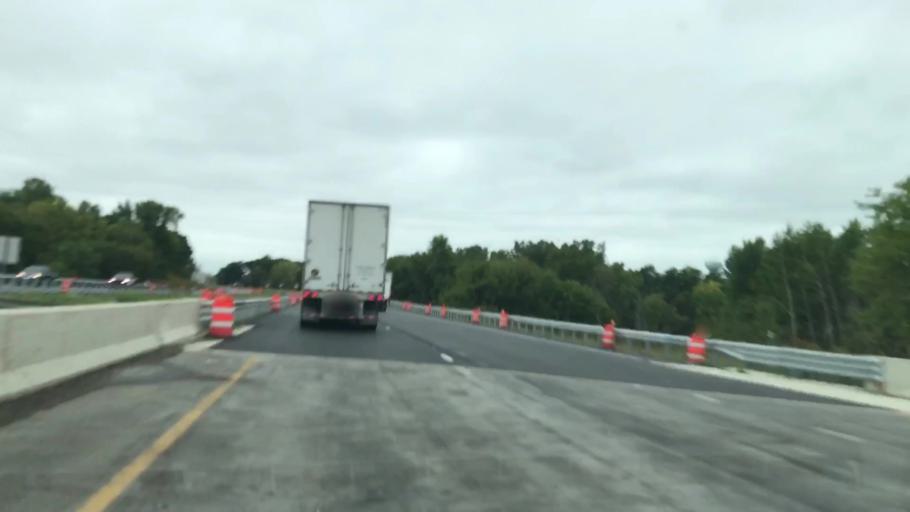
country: US
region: Wisconsin
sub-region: Brown County
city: Suamico
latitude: 44.6315
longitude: -88.0480
